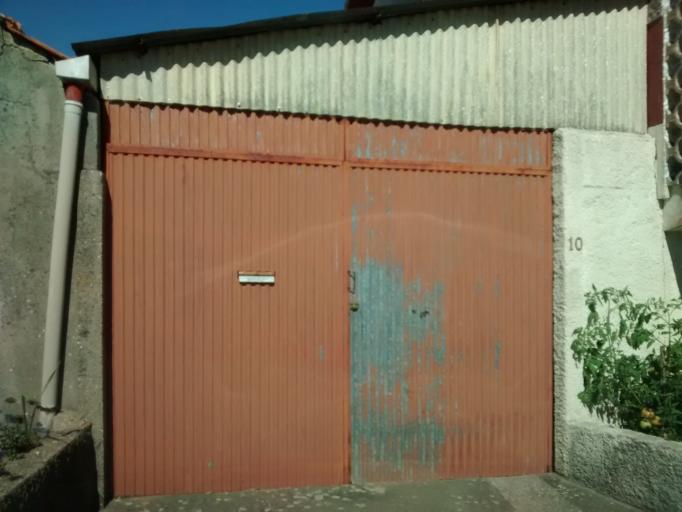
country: PT
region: Aveiro
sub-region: Anadia
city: Sangalhos
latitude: 40.4469
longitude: -8.5048
